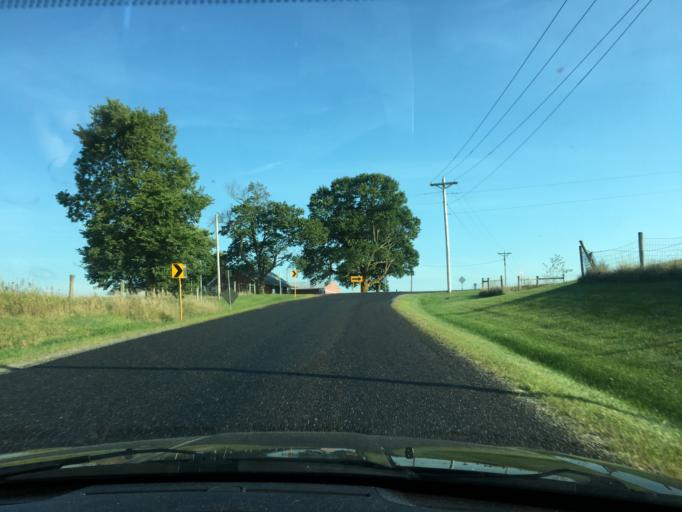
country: US
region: Ohio
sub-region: Logan County
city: West Liberty
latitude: 40.2705
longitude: -83.7224
